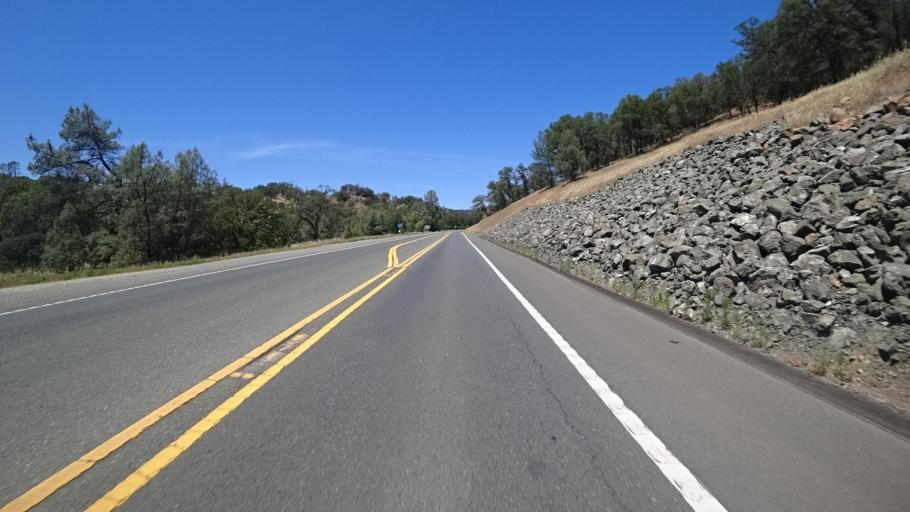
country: US
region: California
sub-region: Lake County
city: Hidden Valley Lake
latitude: 38.8206
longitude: -122.5772
